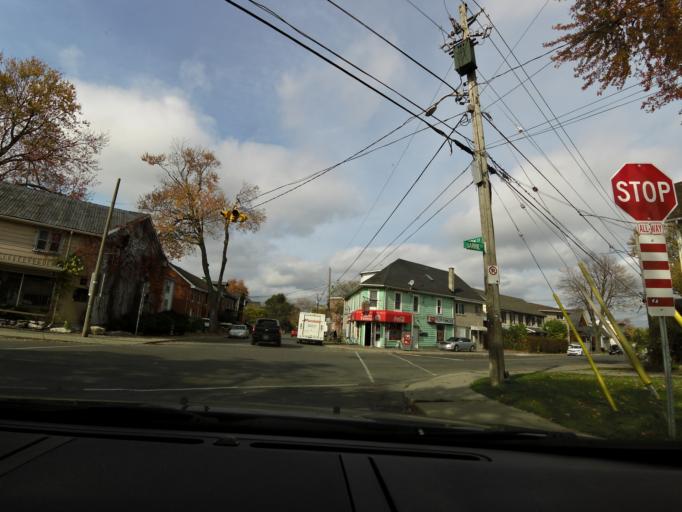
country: CA
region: Ontario
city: Kingston
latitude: 44.2355
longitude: -76.4899
